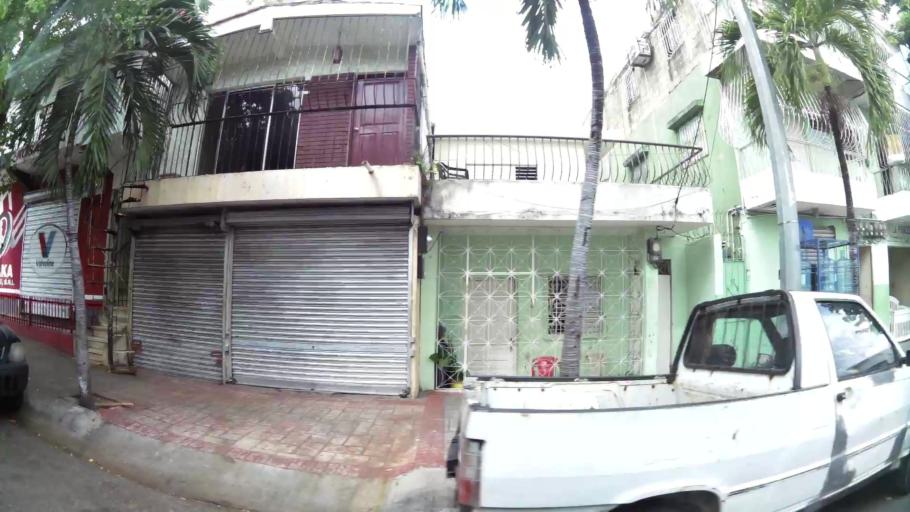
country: DO
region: Nacional
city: San Carlos
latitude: 18.4824
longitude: -69.9045
